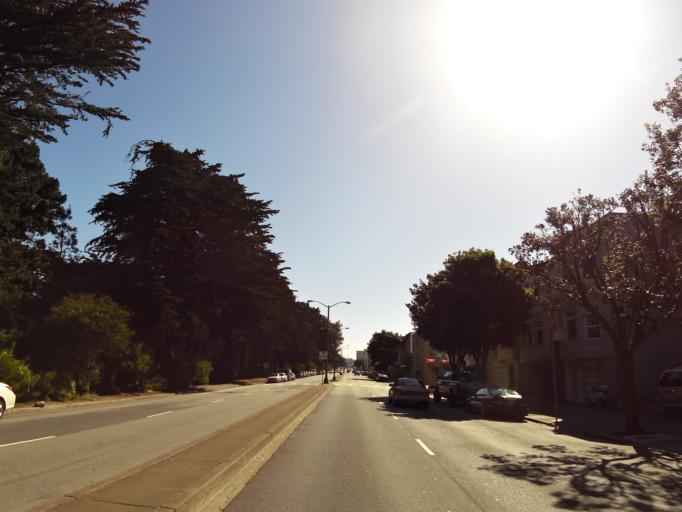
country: US
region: California
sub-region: San Mateo County
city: Daly City
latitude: 37.7652
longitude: -122.4823
